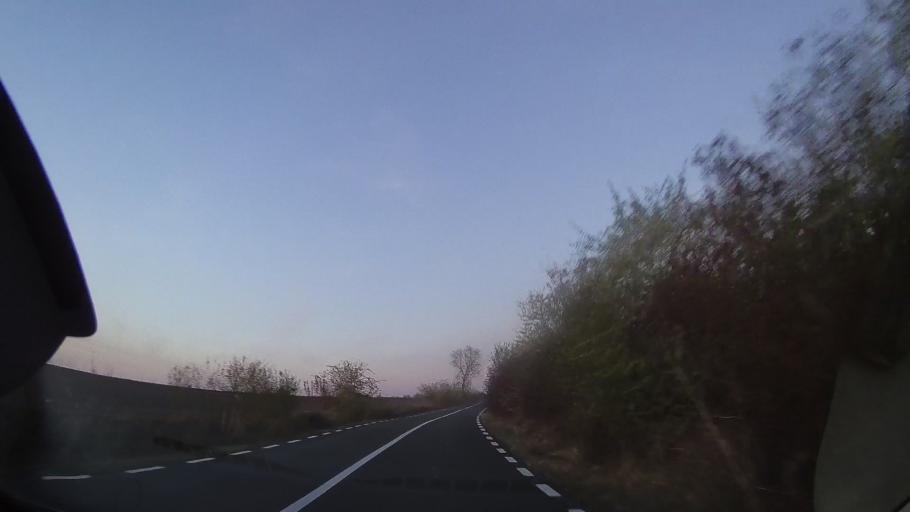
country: RO
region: Constanta
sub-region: Comuna Cobadin
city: Cobadin
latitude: 44.0309
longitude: 28.2612
